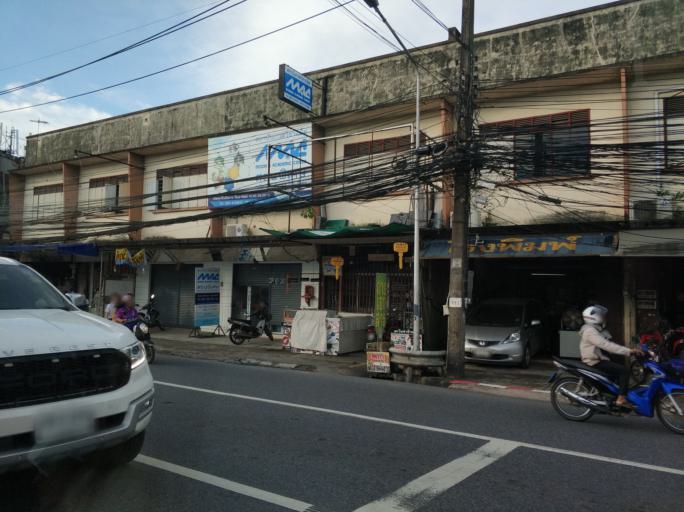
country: TH
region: Phuket
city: Wichit
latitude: 7.8870
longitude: 98.3737
